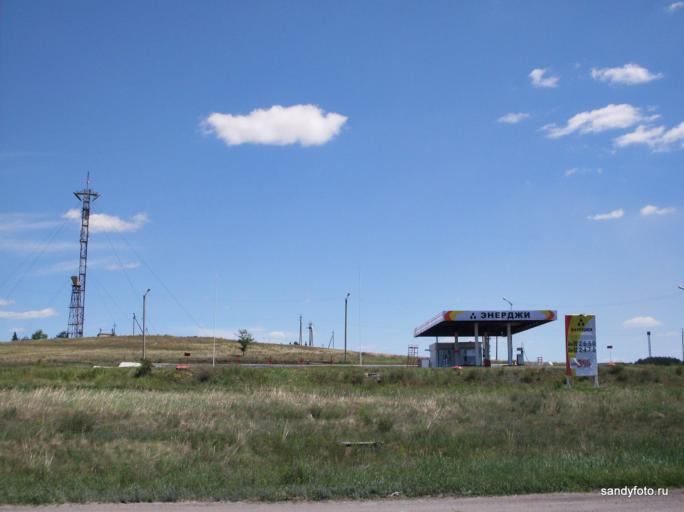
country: RU
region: Chelyabinsk
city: Troitsk
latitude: 54.0740
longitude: 61.6258
